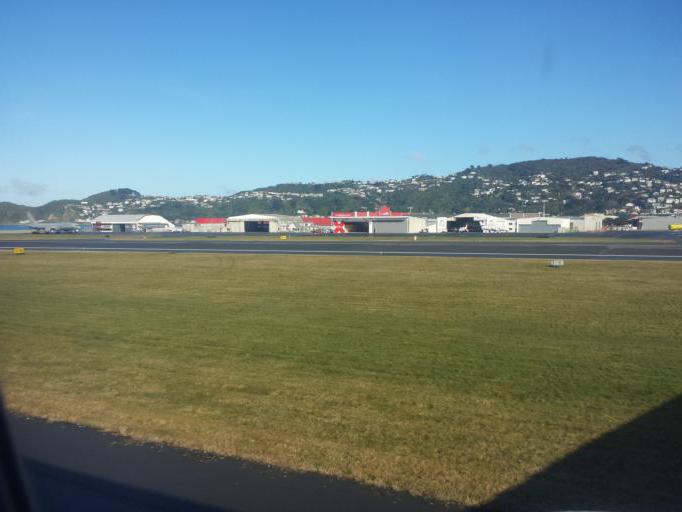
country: NZ
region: Wellington
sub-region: Wellington City
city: Wellington
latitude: -41.3252
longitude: 174.8083
